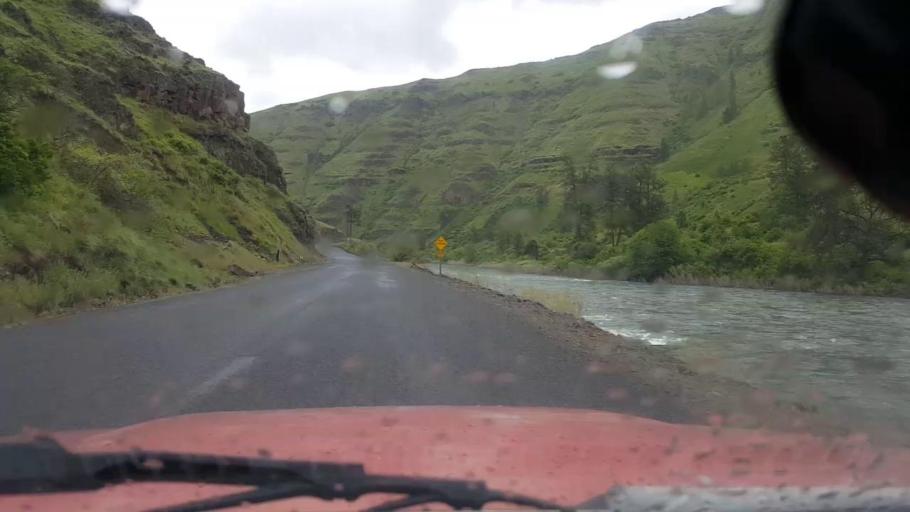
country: US
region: Washington
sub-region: Asotin County
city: Asotin
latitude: 46.0306
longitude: -117.3010
